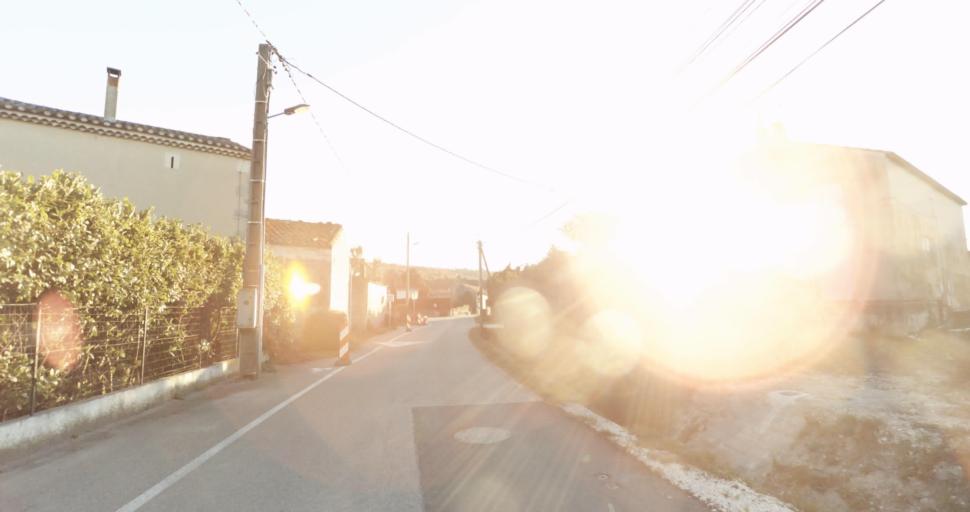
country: FR
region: Provence-Alpes-Cote d'Azur
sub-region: Departement des Bouches-du-Rhone
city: Barbentane
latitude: 43.9046
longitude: 4.7596
